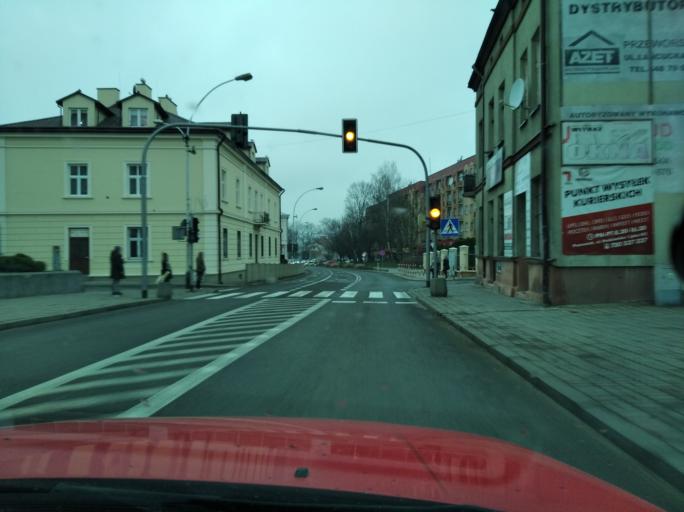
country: PL
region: Subcarpathian Voivodeship
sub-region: Powiat przeworski
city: Przeworsk
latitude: 50.0587
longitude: 22.4905
